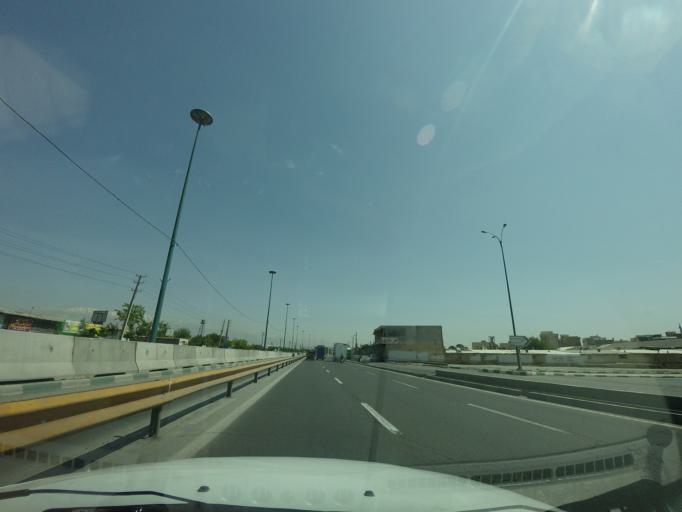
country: IR
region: Tehran
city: Rey
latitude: 35.6256
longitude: 51.3321
